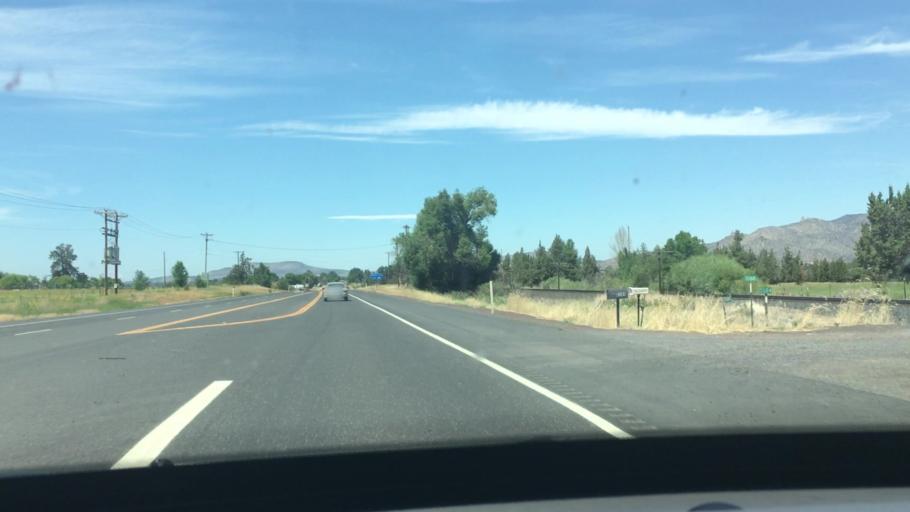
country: US
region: Oregon
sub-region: Deschutes County
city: Terrebonne
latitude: 44.3271
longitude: -121.1760
